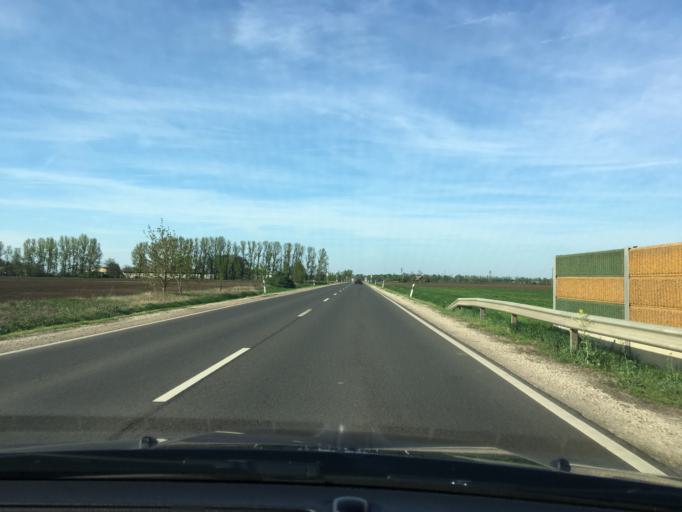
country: HU
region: Bekes
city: Mezobereny
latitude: 46.7993
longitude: 21.0047
